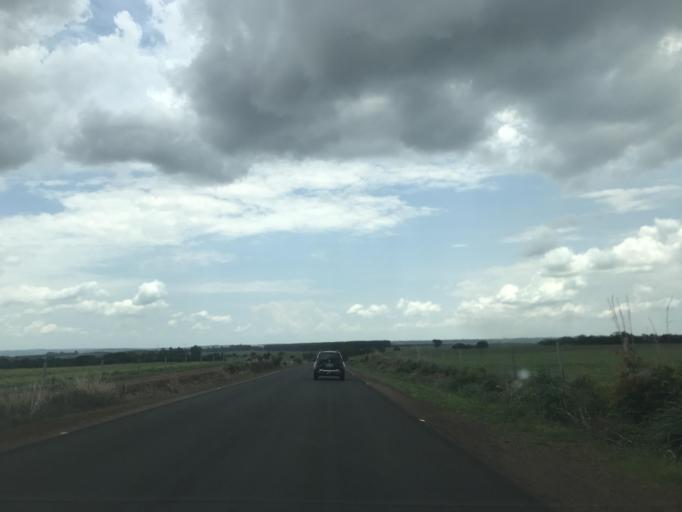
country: BR
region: Goias
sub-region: Vianopolis
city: Vianopolis
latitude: -16.9112
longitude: -48.5538
